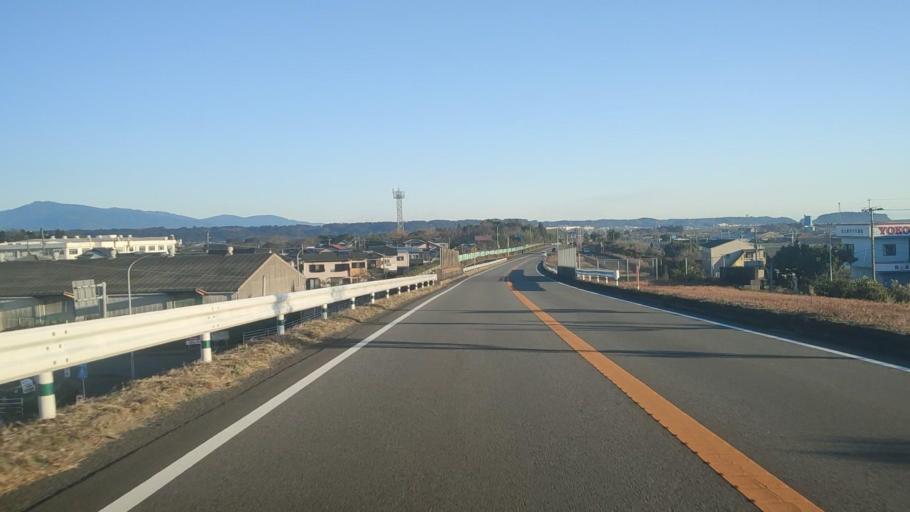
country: JP
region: Miyazaki
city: Tsuma
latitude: 32.0352
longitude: 131.4658
